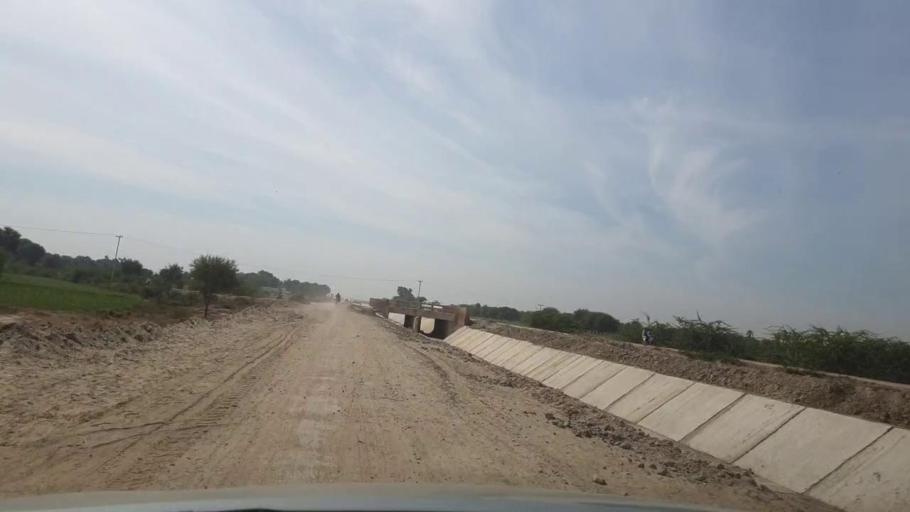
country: PK
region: Sindh
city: Kunri
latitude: 25.1455
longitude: 69.5880
